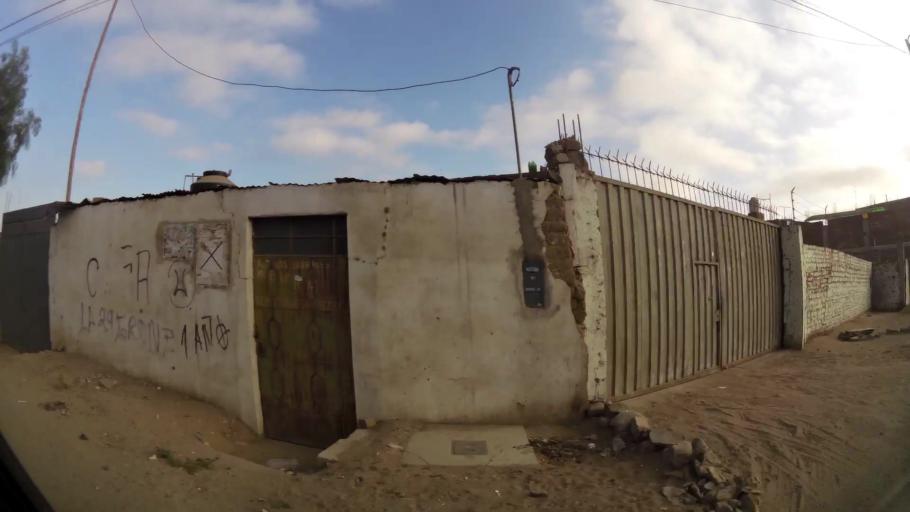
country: PE
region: La Libertad
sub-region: Provincia de Trujillo
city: El Porvenir
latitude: -8.0885
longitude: -79.0202
